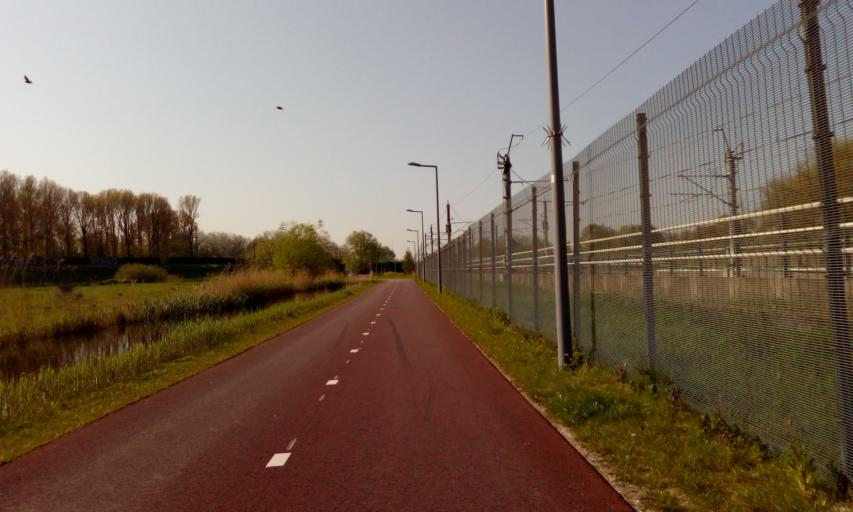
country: NL
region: South Holland
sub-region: Gemeente Rotterdam
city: Rotterdam
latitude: 51.9382
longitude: 4.4515
